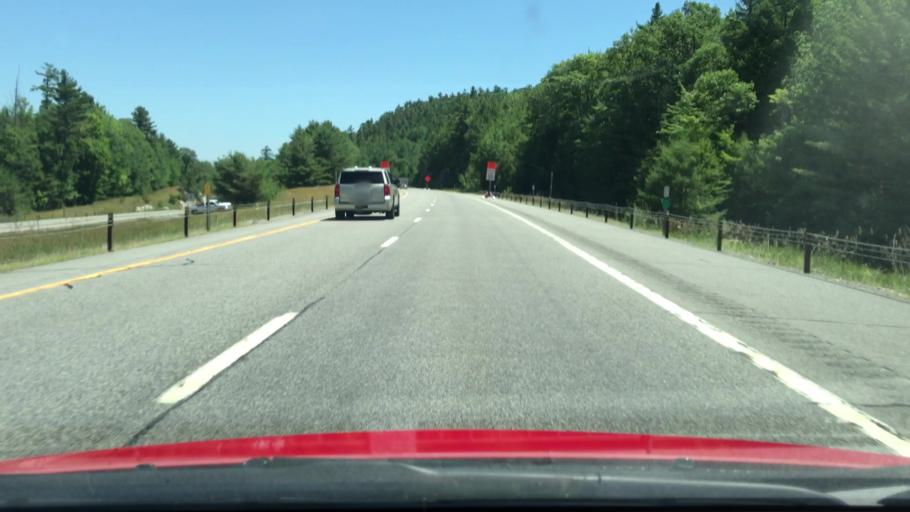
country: US
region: New York
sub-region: Essex County
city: Elizabethtown
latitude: 44.1979
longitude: -73.5206
